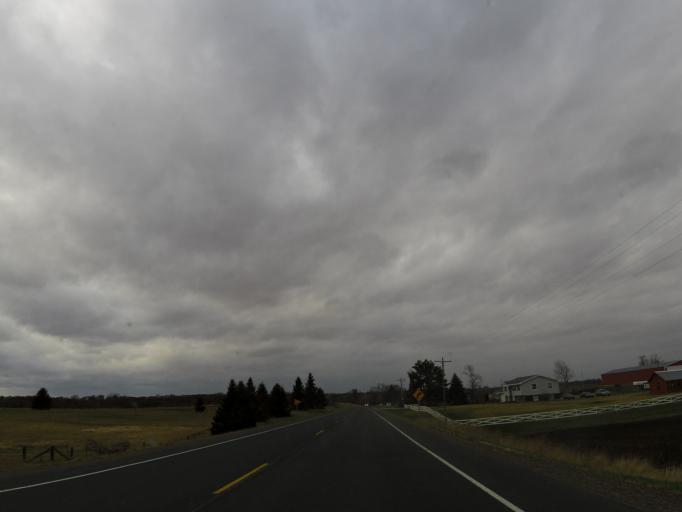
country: US
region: Wisconsin
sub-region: Saint Croix County
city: New Richmond
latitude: 45.0873
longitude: -92.5732
